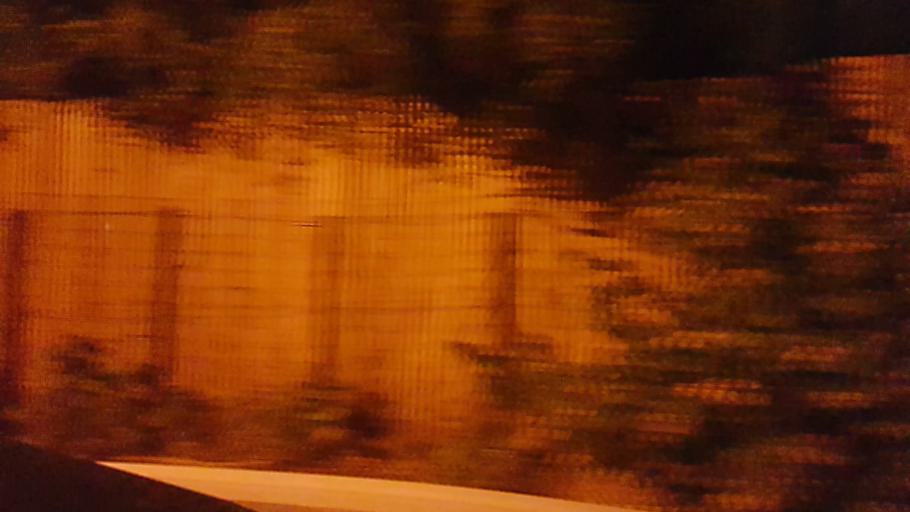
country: IL
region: Central District
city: Hod HaSharon
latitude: 32.1672
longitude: 34.8897
